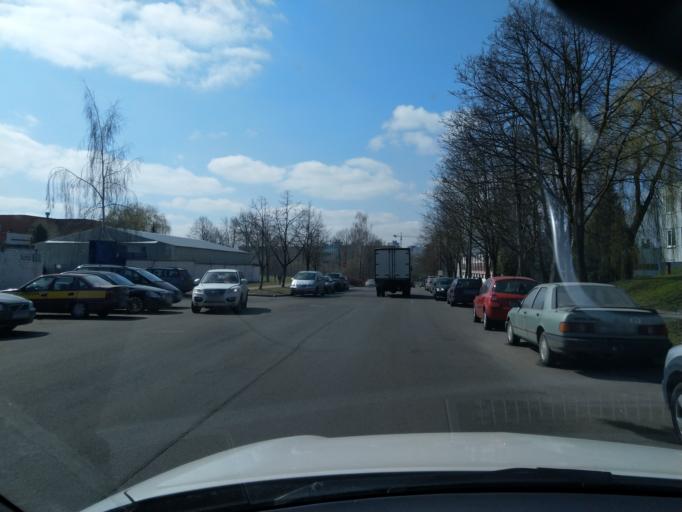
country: BY
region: Minsk
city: Syenitsa
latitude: 53.8650
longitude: 27.5053
